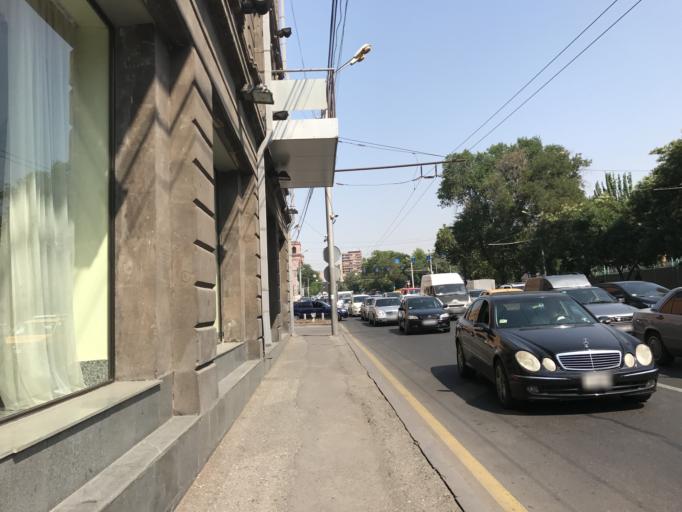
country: AM
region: Yerevan
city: Yerevan
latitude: 40.1734
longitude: 44.5065
